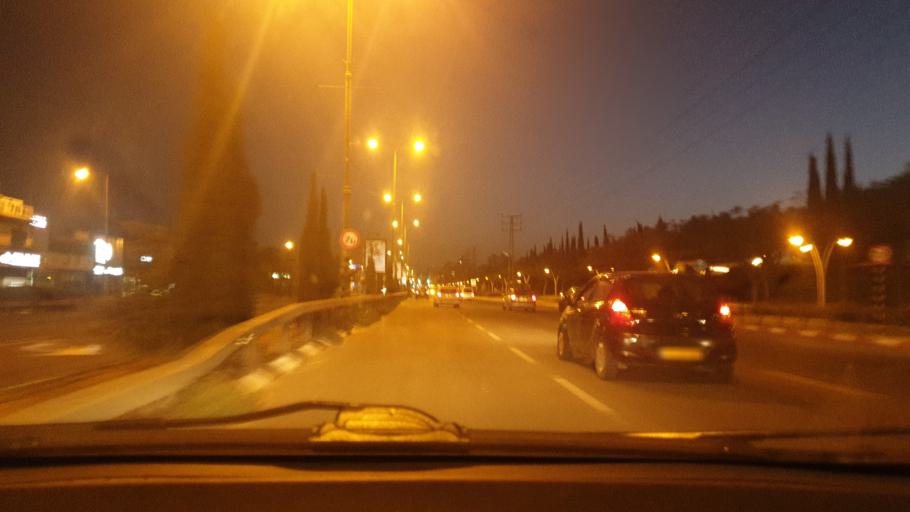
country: IL
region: Central District
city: Rishon LeZiyyon
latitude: 31.9805
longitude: 34.8091
